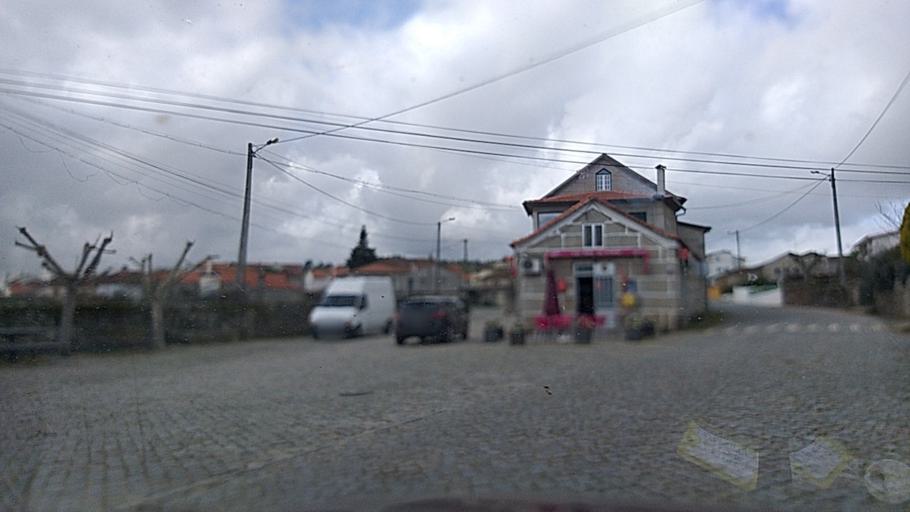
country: PT
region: Guarda
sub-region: Fornos de Algodres
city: Fornos de Algodres
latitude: 40.6621
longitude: -7.5652
